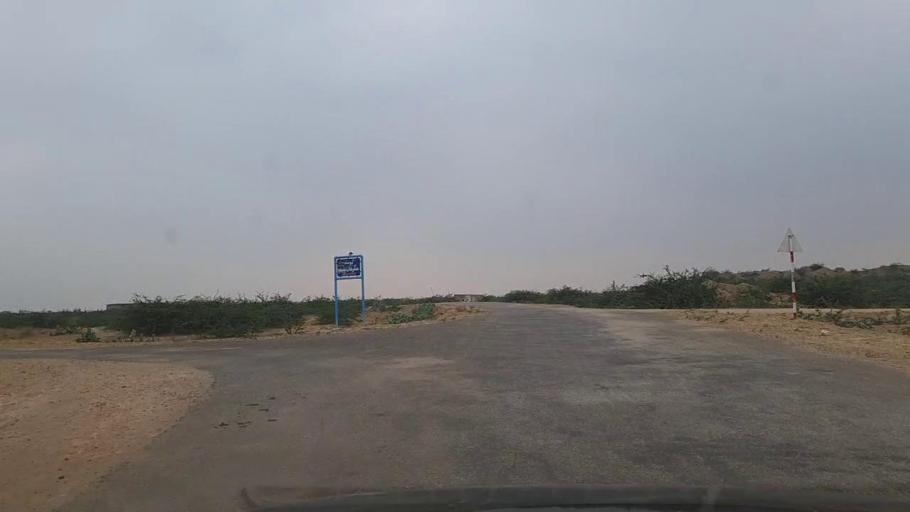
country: PK
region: Sindh
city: Thatta
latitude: 24.8505
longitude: 67.7693
